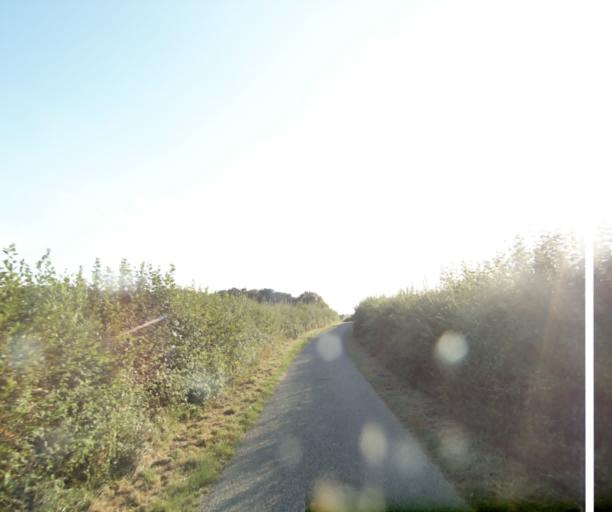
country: FR
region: Bourgogne
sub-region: Departement de Saone-et-Loire
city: Gueugnon
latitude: 46.5820
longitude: 4.1360
